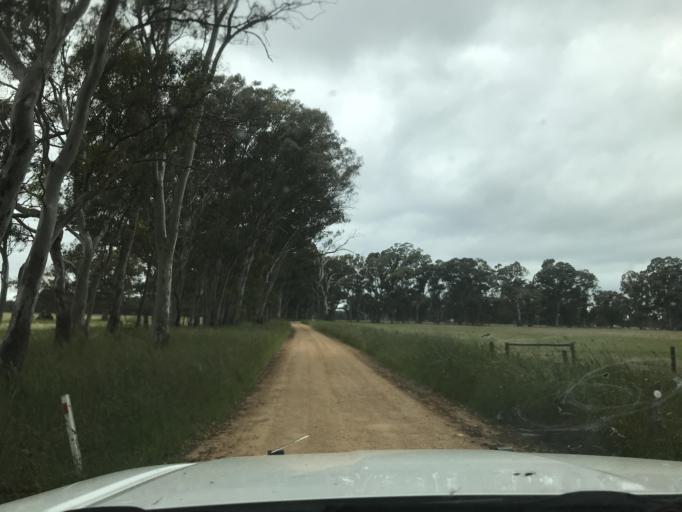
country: AU
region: South Australia
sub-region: Wattle Range
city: Penola
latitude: -37.2705
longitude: 140.9771
